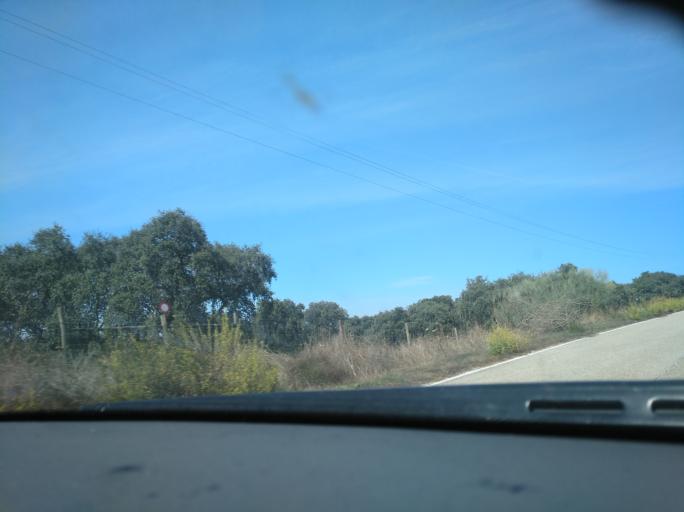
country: PT
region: Evora
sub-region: Montemor-O-Novo
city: Montemor-o-Novo
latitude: 38.6663
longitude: -8.0945
